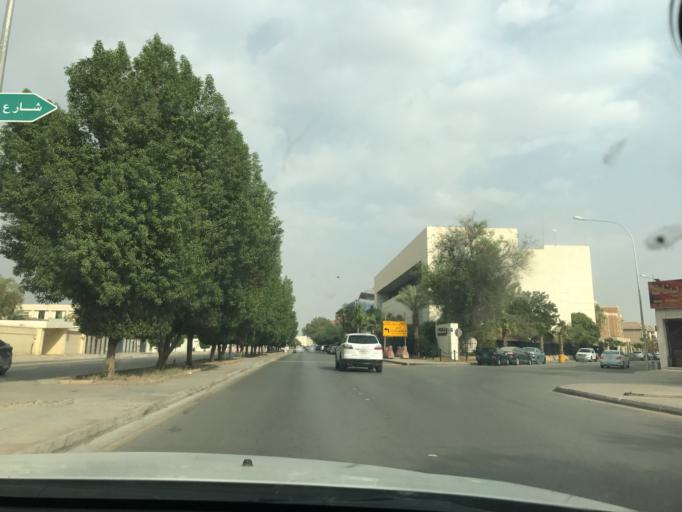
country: SA
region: Ar Riyad
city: Riyadh
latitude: 24.7066
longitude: 46.7091
